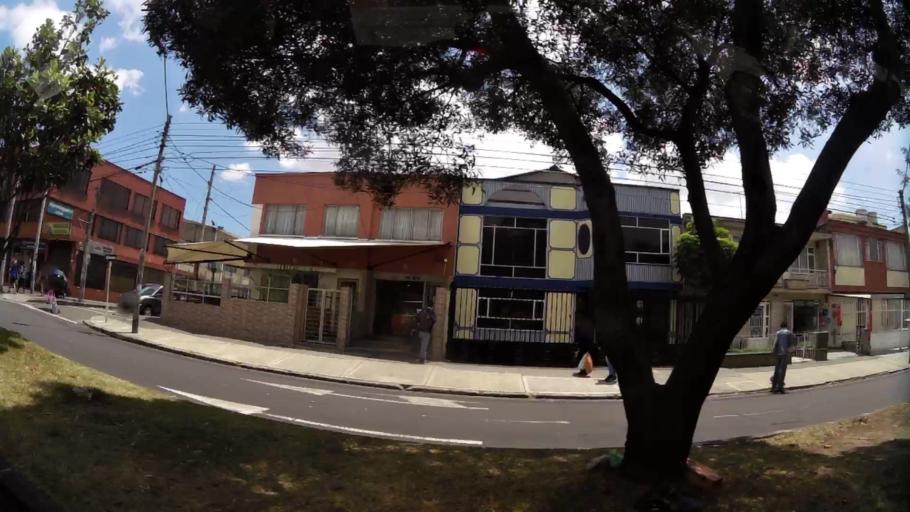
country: CO
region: Bogota D.C.
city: Bogota
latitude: 4.5810
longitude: -74.0958
